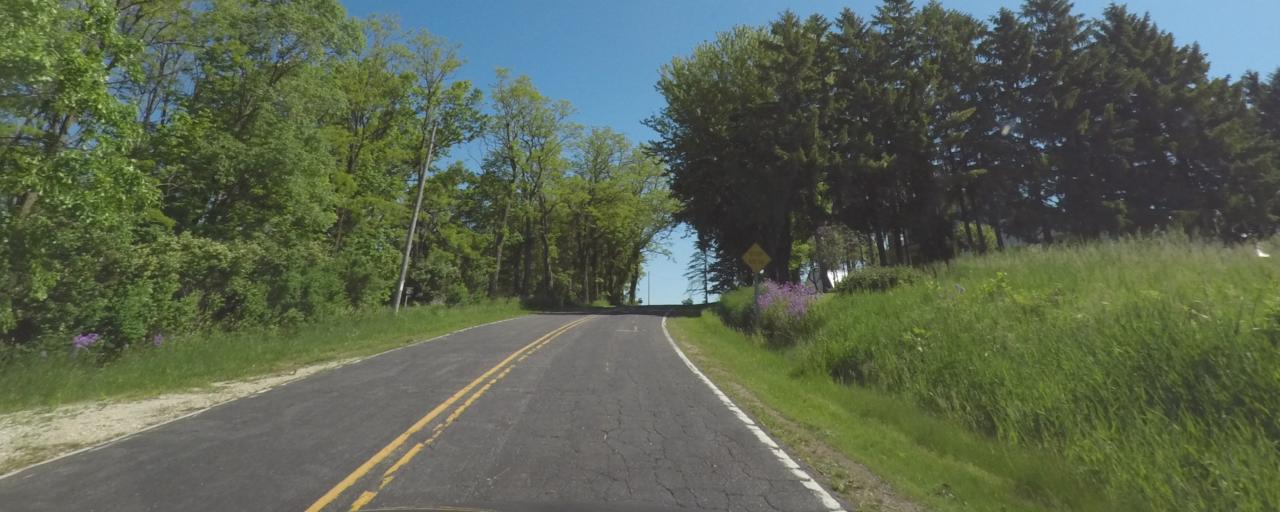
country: US
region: Wisconsin
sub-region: Sheboygan County
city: Sheboygan Falls
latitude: 43.7487
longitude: -87.8396
